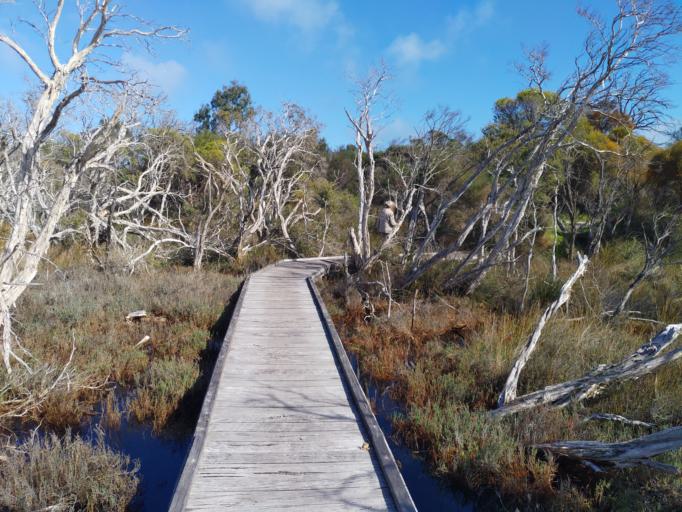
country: AU
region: Western Australia
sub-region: Mandurah
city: Erskine
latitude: -32.5696
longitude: 115.6894
